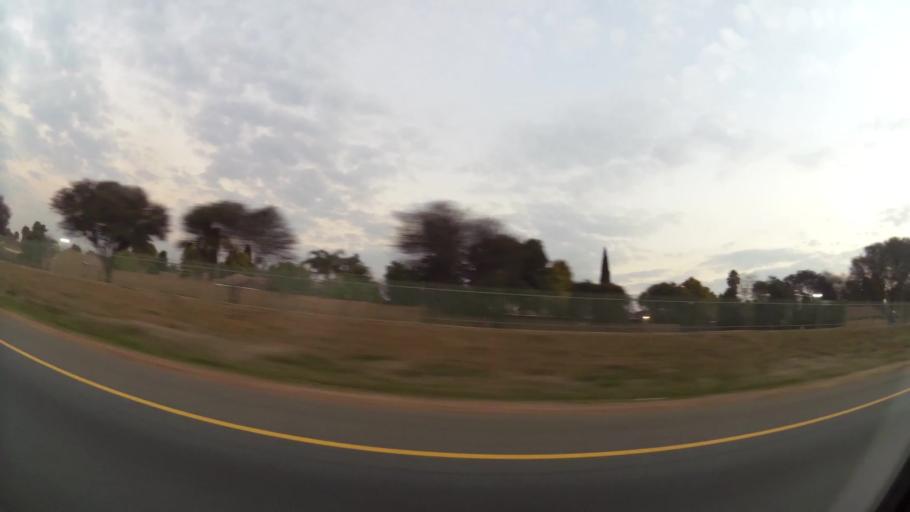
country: ZA
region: Gauteng
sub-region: Ekurhuleni Metropolitan Municipality
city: Boksburg
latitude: -26.2519
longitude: 28.2631
